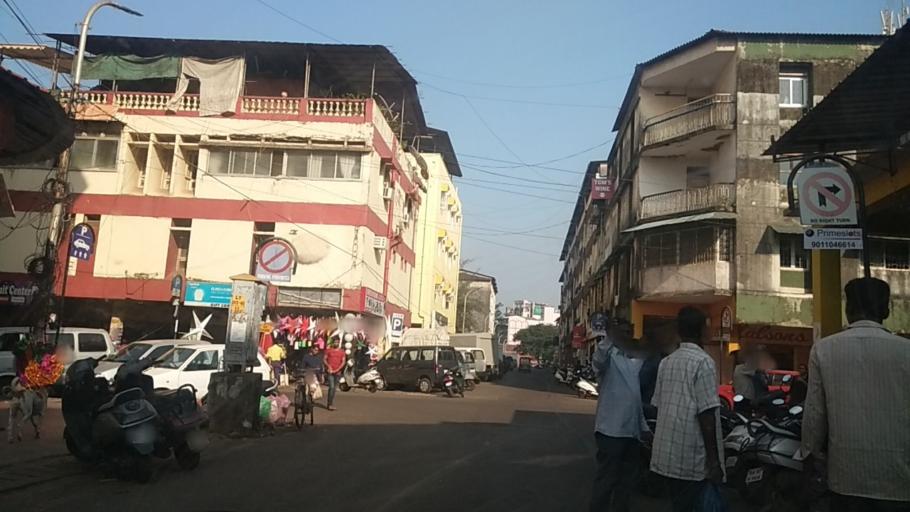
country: IN
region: Goa
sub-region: North Goa
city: Panaji
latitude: 15.4986
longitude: 73.8229
